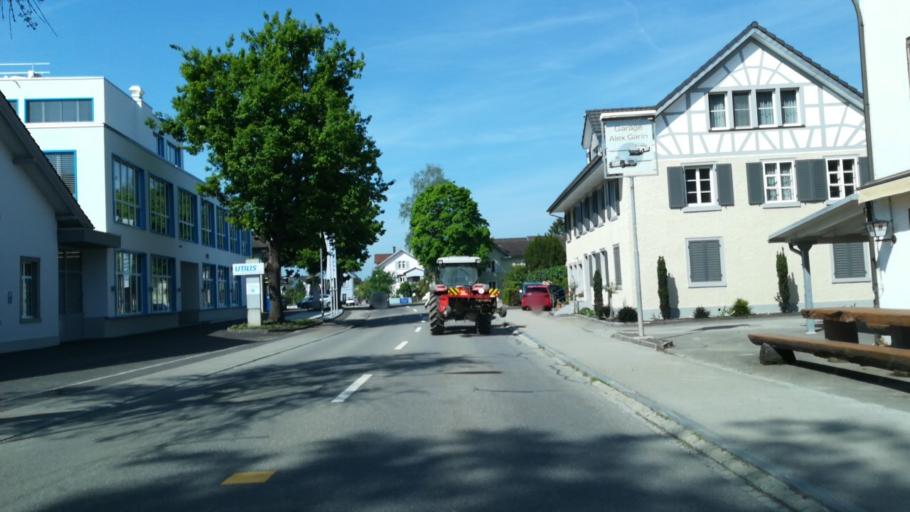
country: CH
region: Thurgau
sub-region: Frauenfeld District
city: Mullheim
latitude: 47.6037
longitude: 9.0059
